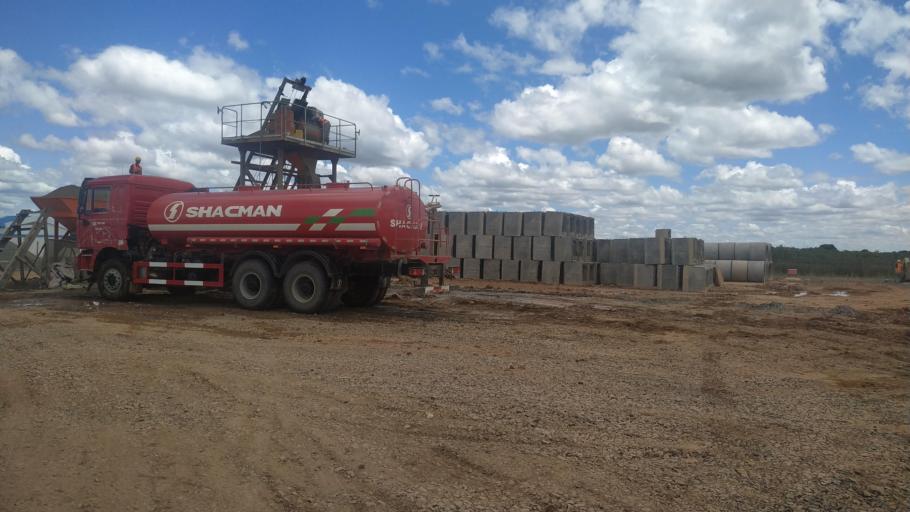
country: MG
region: Analamanga
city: Anjozorobe
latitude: -18.2747
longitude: 48.2634
